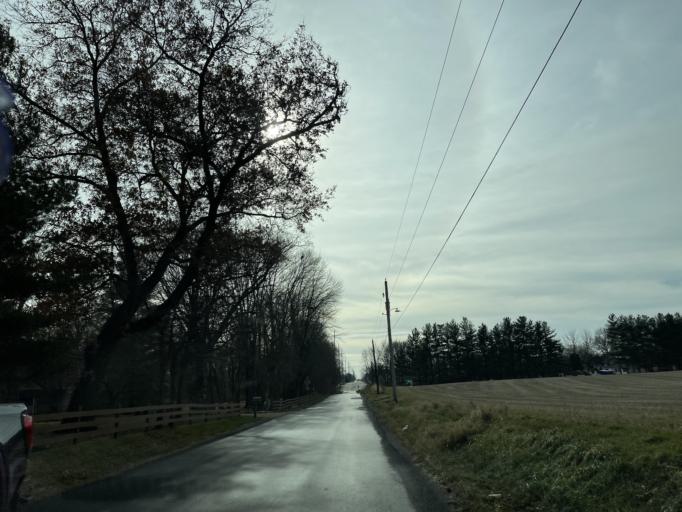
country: US
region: Illinois
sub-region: Sangamon County
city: Leland Grove
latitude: 39.7803
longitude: -89.7347
